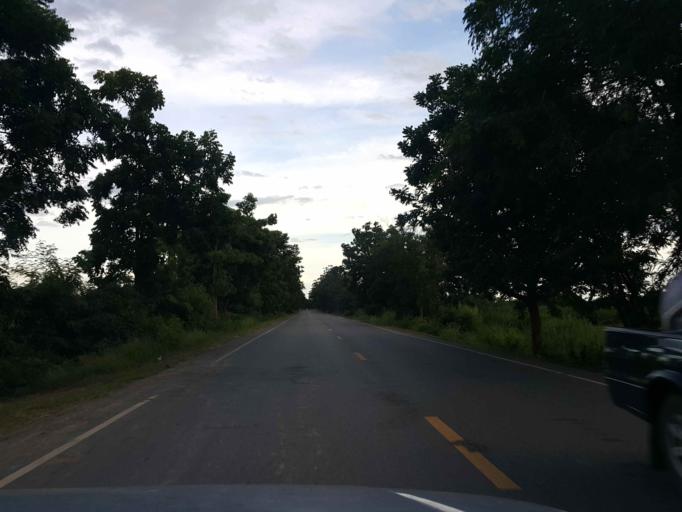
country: TH
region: Sukhothai
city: Sawankhalok
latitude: 17.3774
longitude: 99.7386
